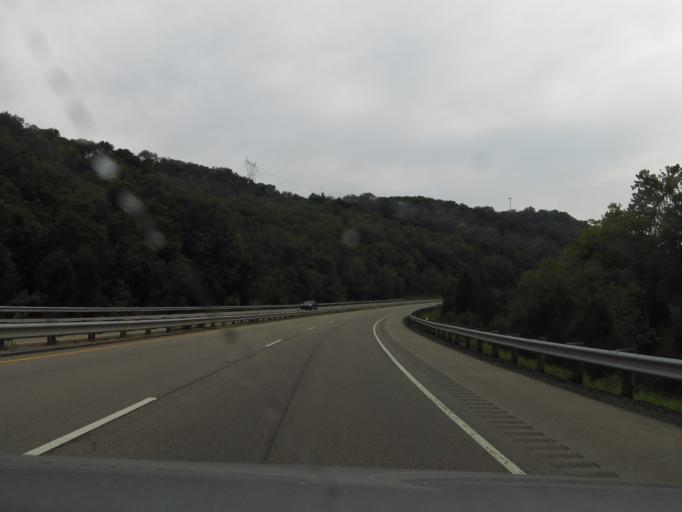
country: US
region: Ohio
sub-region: Brown County
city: Ripley
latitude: 38.7643
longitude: -83.8149
